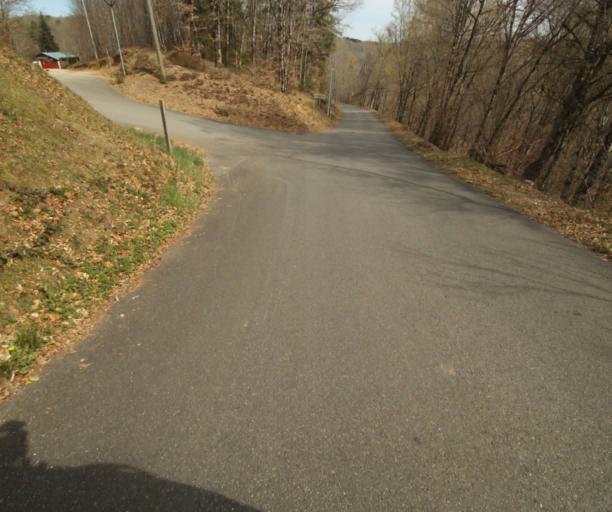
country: FR
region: Limousin
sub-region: Departement de la Correze
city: Naves
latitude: 45.3415
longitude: 1.8111
